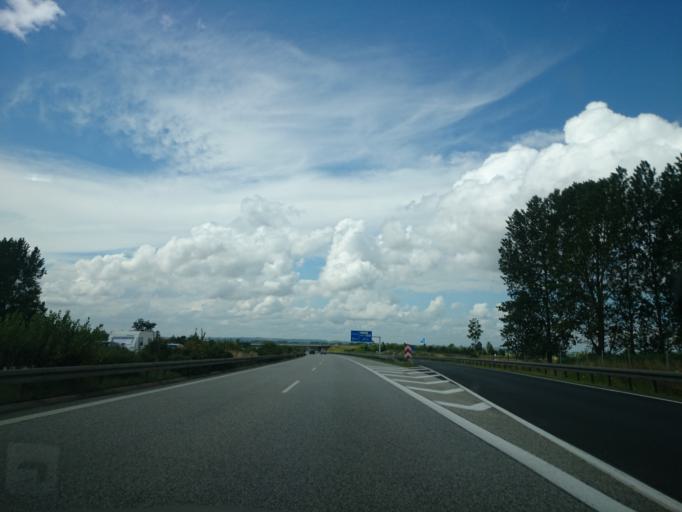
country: DE
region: Mecklenburg-Vorpommern
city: Hornstorf
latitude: 53.8798
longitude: 11.5419
